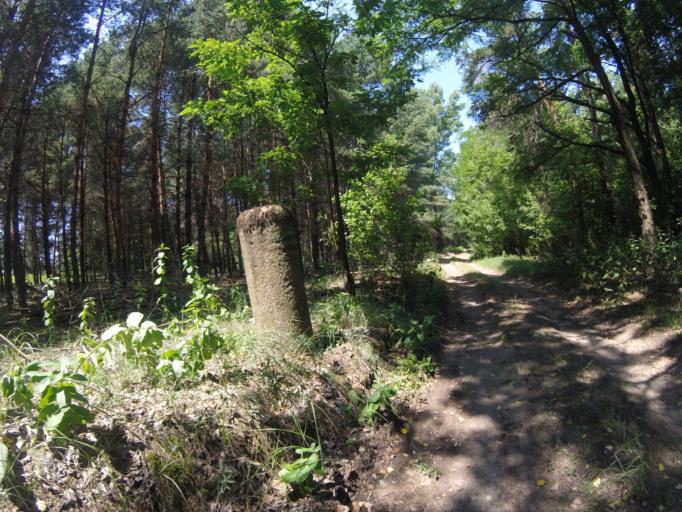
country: HU
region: Bacs-Kiskun
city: Jaszszentlaszlo
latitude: 46.6210
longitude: 19.7178
